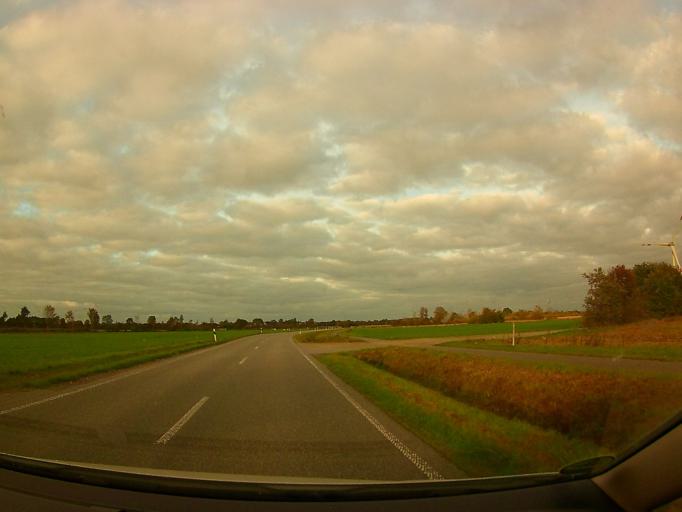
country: DE
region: Schleswig-Holstein
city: Silberstedt
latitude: 54.5246
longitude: 9.3862
